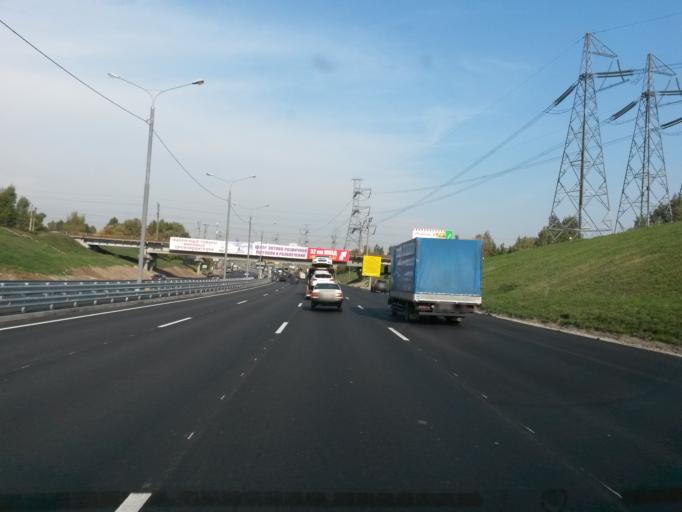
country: RU
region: Moscow
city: Annino
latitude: 55.5625
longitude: 37.6045
